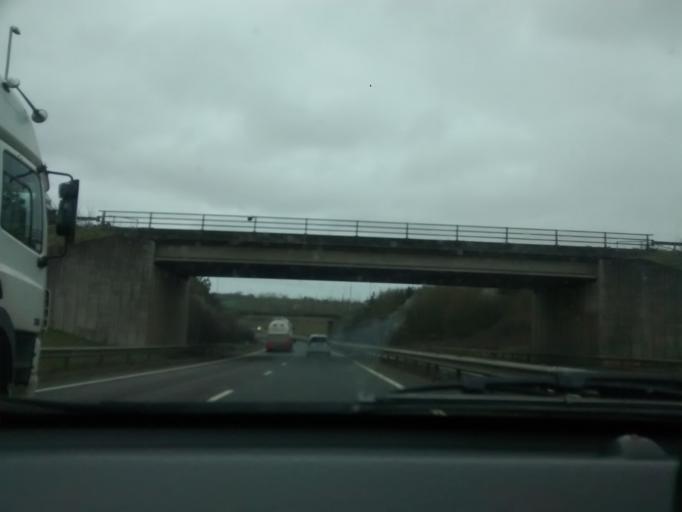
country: GB
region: England
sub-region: Suffolk
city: Bramford
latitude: 52.0371
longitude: 1.0976
